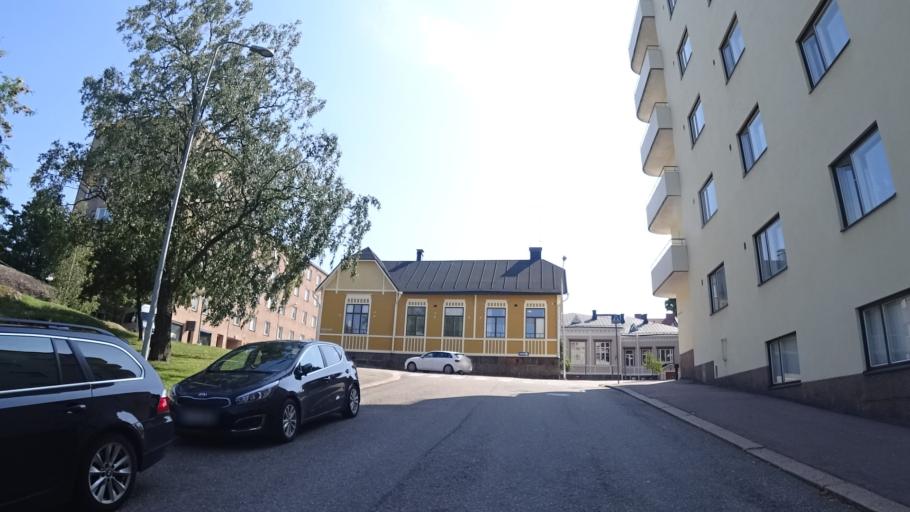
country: FI
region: Kymenlaakso
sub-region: Kotka-Hamina
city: Kotka
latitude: 60.4663
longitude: 26.9385
